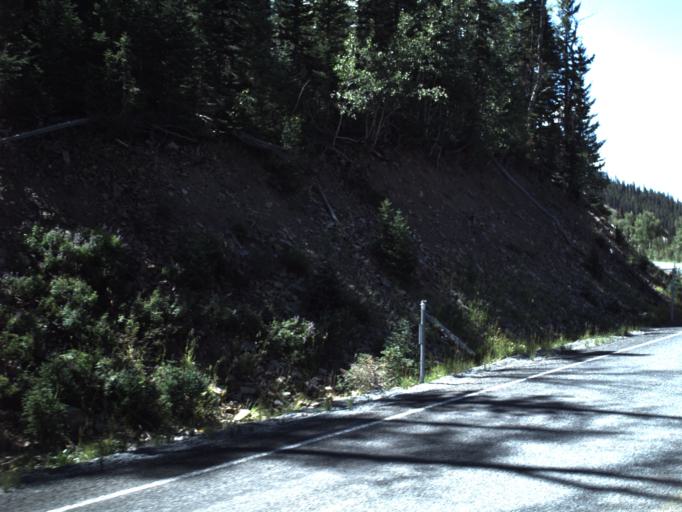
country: US
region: Utah
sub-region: Piute County
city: Junction
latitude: 38.3253
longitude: -112.3717
